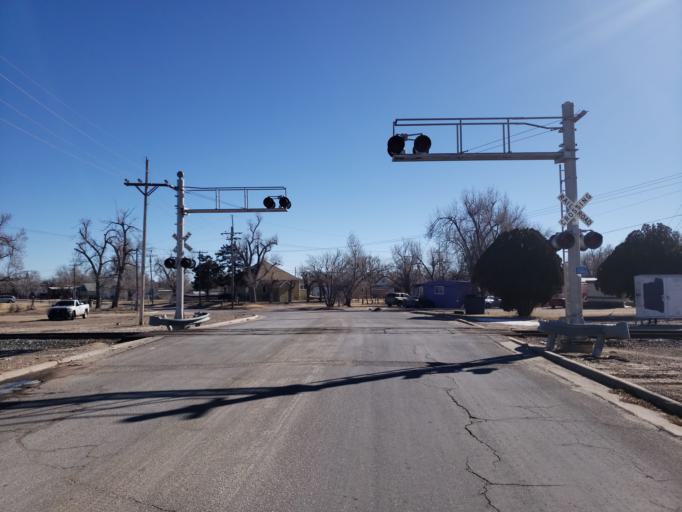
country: US
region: Kansas
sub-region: Ford County
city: Dodge City
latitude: 37.7398
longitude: -100.0293
